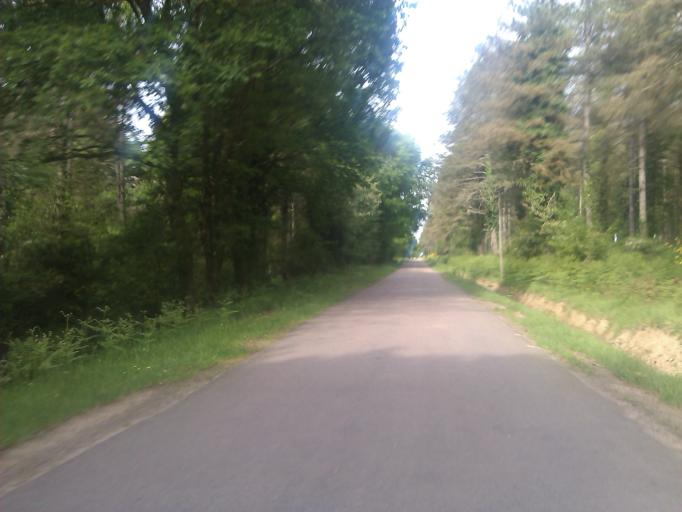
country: FR
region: Auvergne
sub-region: Departement de l'Allier
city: Ainay-le-Chateau
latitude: 46.6135
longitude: 2.6750
